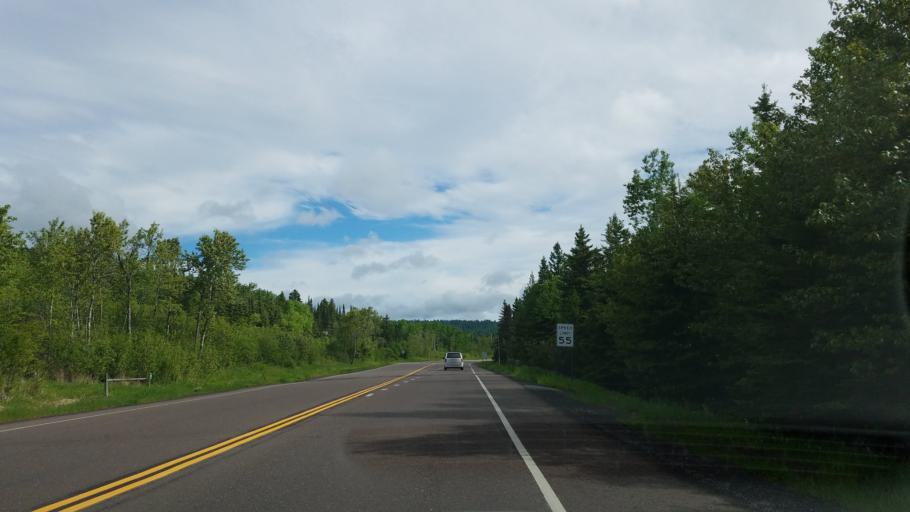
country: US
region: Minnesota
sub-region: Lake County
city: Two Harbors
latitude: 47.0781
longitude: -91.5857
